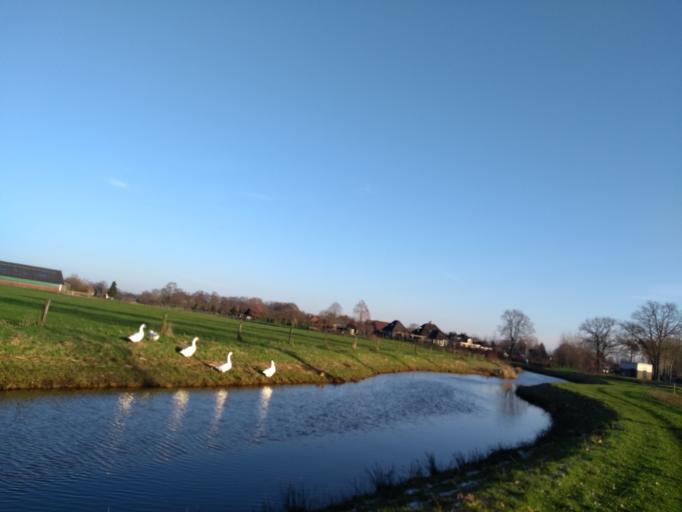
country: NL
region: Overijssel
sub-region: Gemeente Almelo
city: Almelo
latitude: 52.3762
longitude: 6.7153
